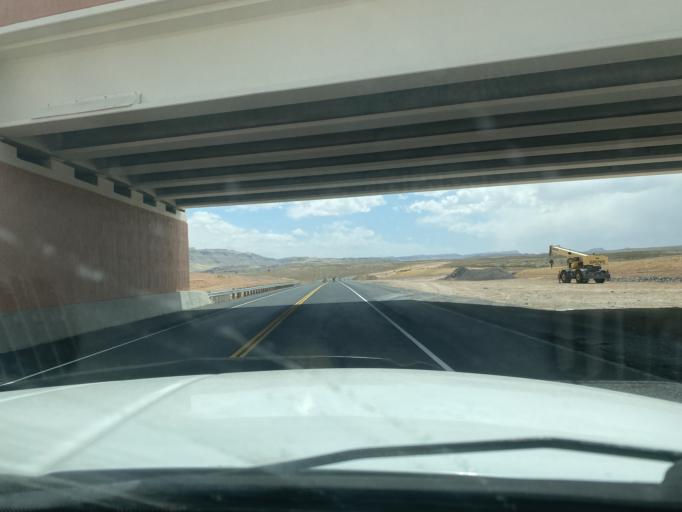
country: US
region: Utah
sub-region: Washington County
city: Hurricane
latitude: 37.1271
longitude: -113.3455
